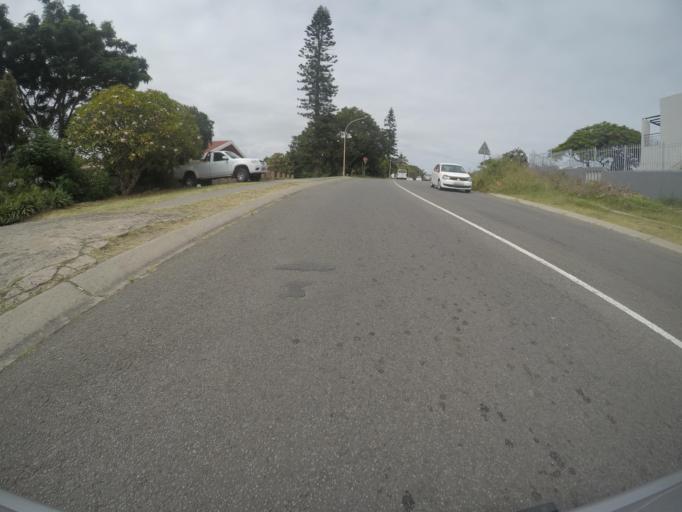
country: ZA
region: Eastern Cape
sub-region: Buffalo City Metropolitan Municipality
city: East London
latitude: -33.0019
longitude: 27.8850
